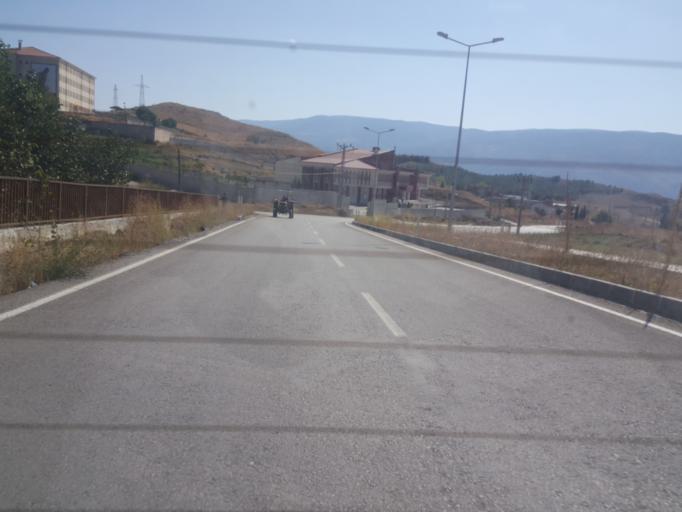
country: TR
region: Kastamonu
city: Tosya
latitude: 41.0061
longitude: 34.0636
